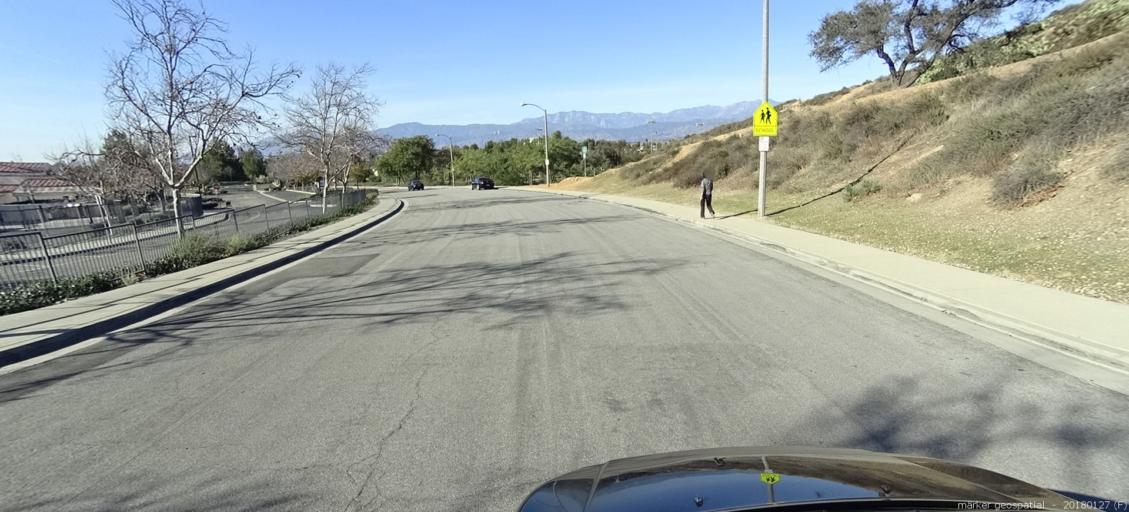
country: US
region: California
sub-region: Los Angeles County
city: Diamond Bar
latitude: 34.0110
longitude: -117.7900
